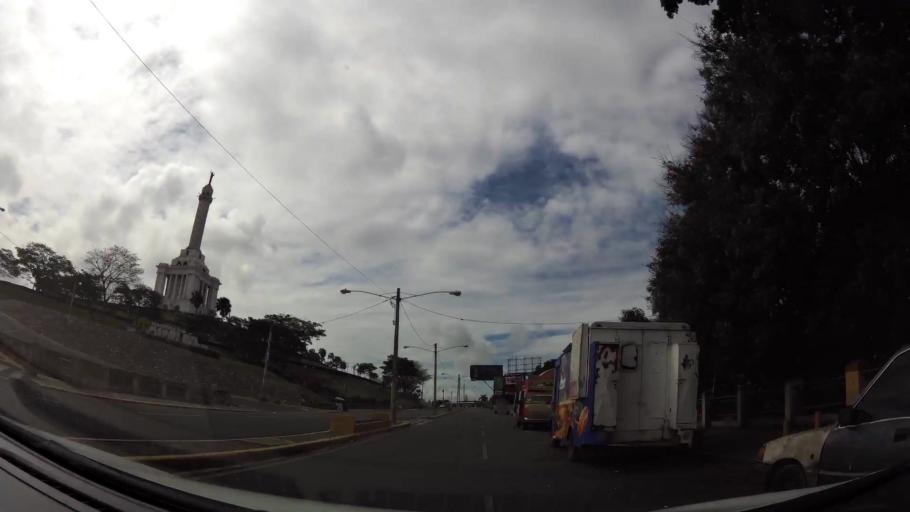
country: DO
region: Santiago
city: Santiago de los Caballeros
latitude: 19.4524
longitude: -70.6955
